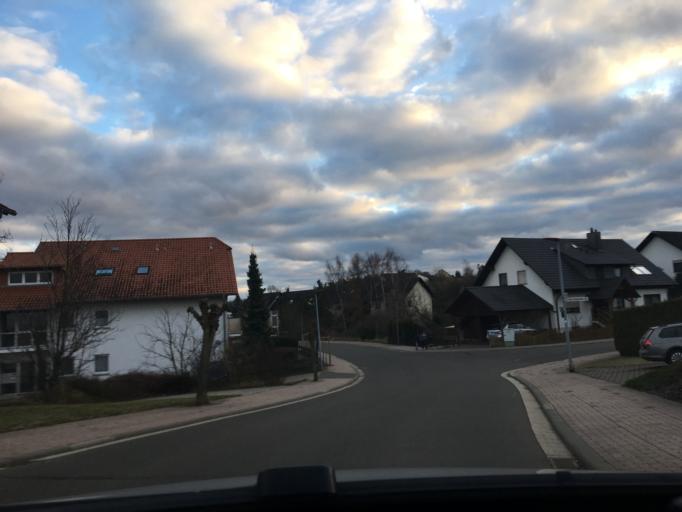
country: DE
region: Rheinland-Pfalz
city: Kirchheimbolanden
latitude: 49.6714
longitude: 7.9969
